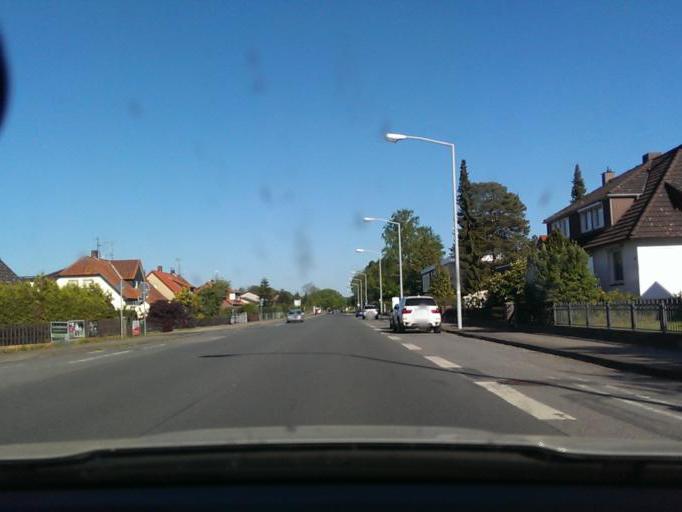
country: DE
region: Lower Saxony
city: Wietze
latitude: 52.6472
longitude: 9.8619
